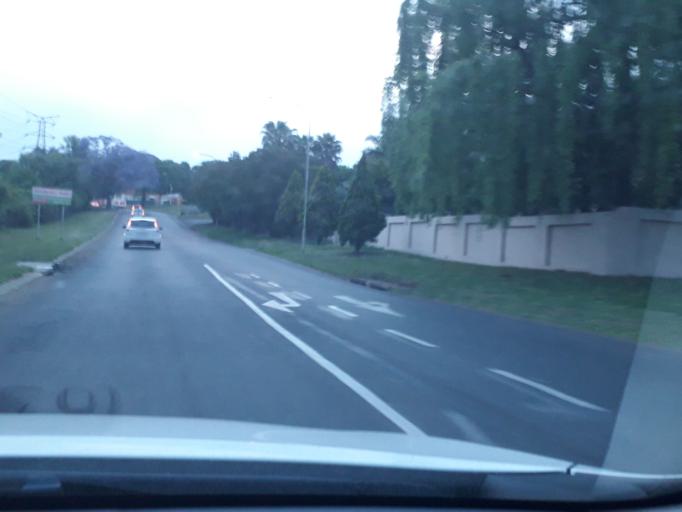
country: ZA
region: Gauteng
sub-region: City of Johannesburg Metropolitan Municipality
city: Johannesburg
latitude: -26.1493
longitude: 27.9940
